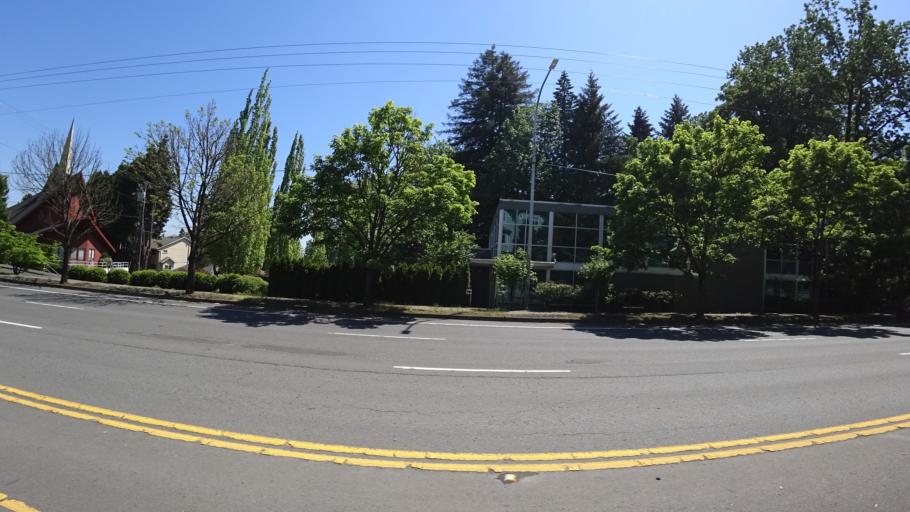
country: US
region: Oregon
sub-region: Multnomah County
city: Portland
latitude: 45.4905
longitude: -122.6797
